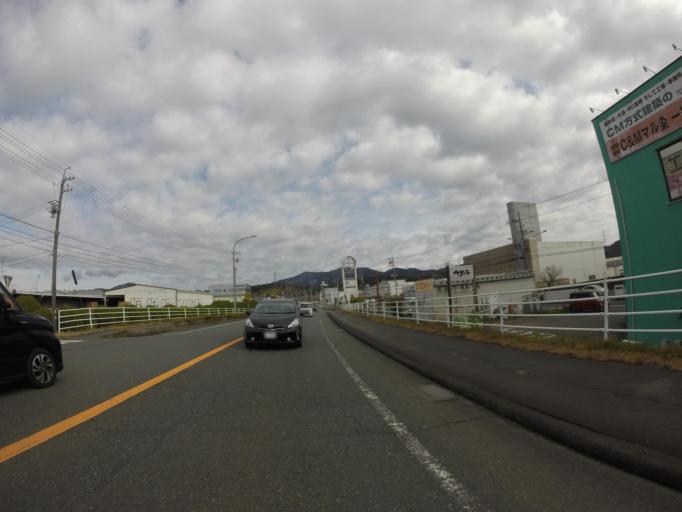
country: JP
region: Shizuoka
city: Hamakita
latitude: 34.8111
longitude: 137.6851
